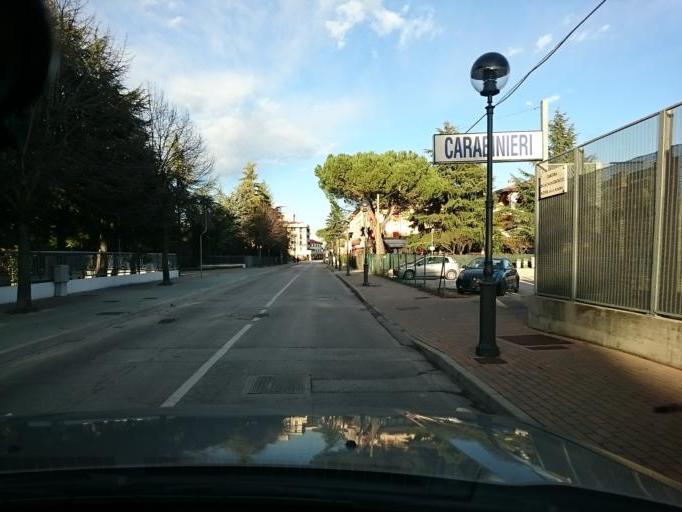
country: IT
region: Veneto
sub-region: Provincia di Padova
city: Montegrotto Terme
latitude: 45.3250
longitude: 11.7931
